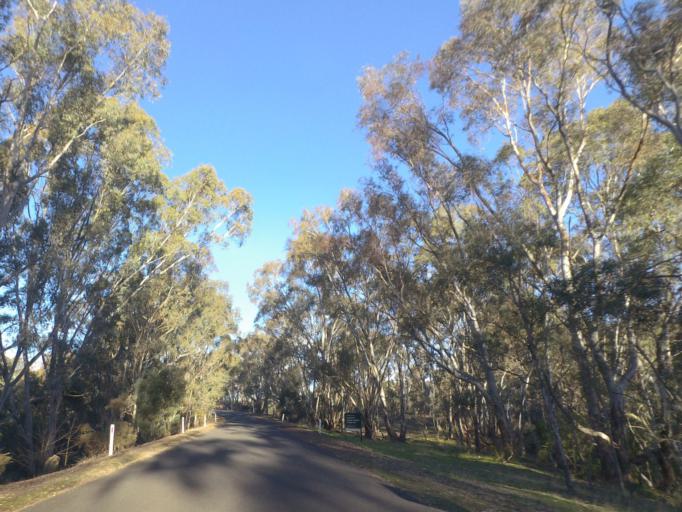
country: AU
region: Victoria
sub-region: Mount Alexander
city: Castlemaine
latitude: -37.1575
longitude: 144.2107
